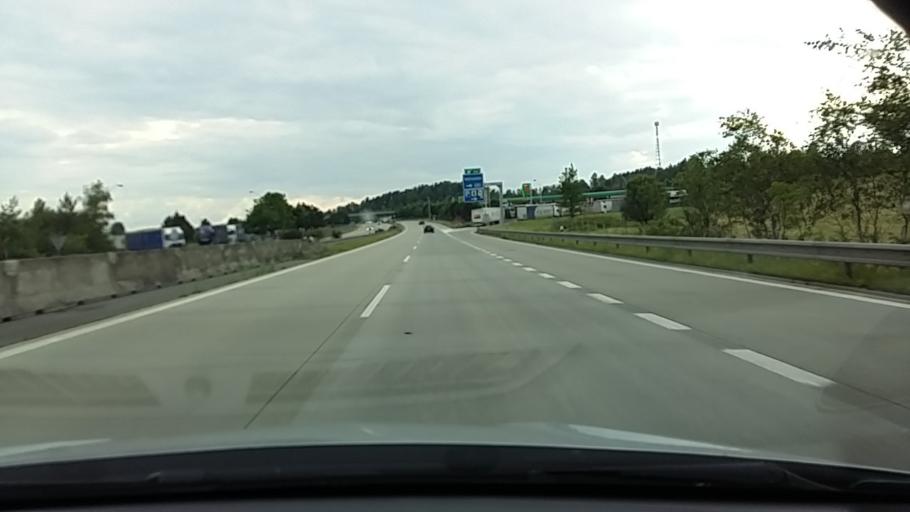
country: CZ
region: Plzensky
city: Primda
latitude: 49.6786
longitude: 12.6069
